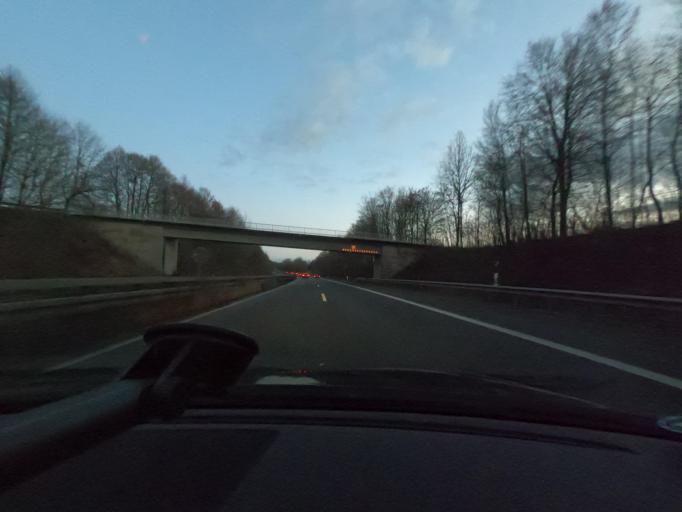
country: DE
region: Lower Saxony
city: Herzberg am Harz
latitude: 51.6461
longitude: 10.3505
